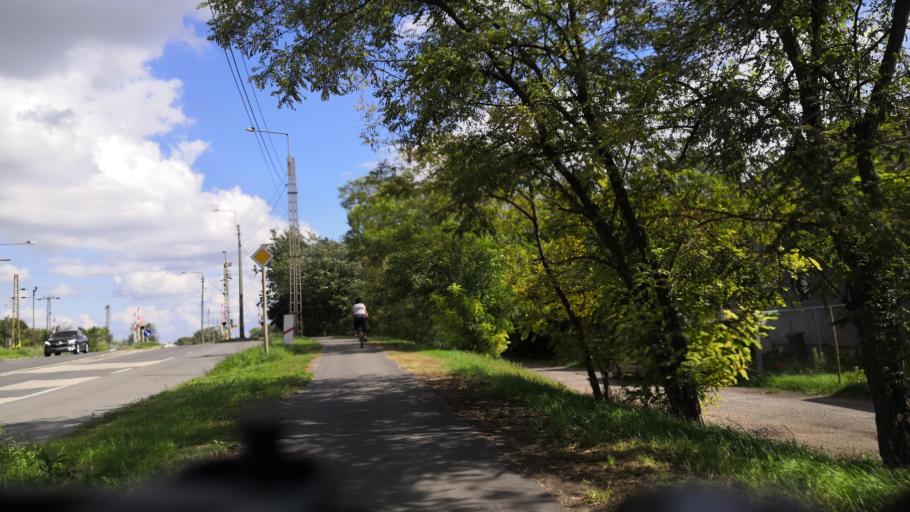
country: HU
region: Csongrad
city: Szeged
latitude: 46.2699
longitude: 20.0909
